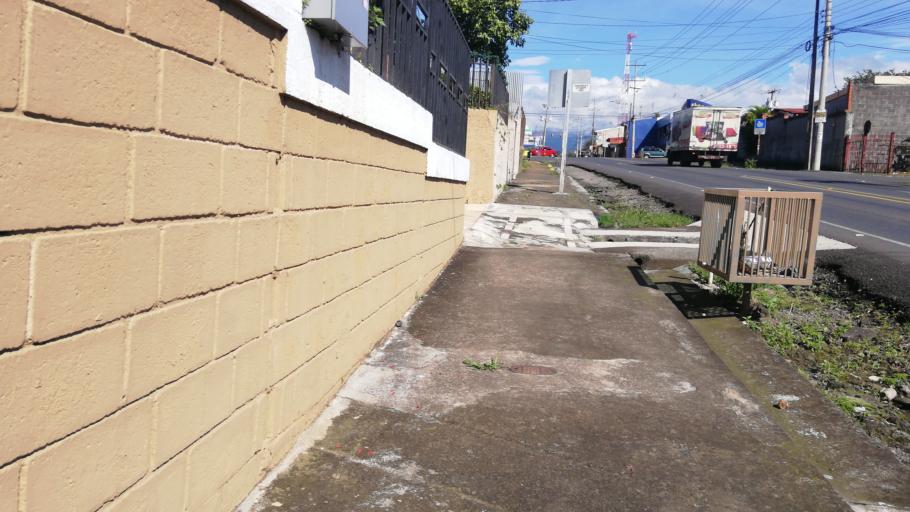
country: CR
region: Alajuela
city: San Juan
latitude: 10.0715
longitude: -84.3083
